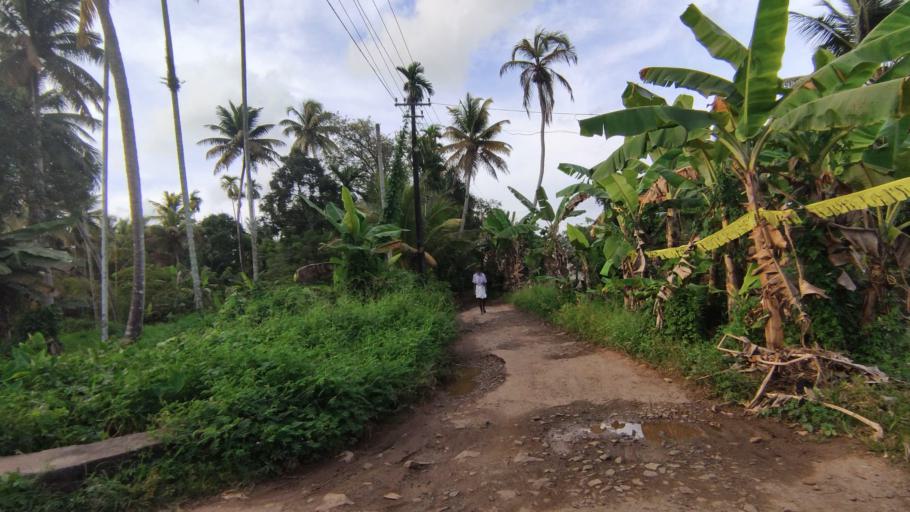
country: IN
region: Kerala
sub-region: Kottayam
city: Kottayam
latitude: 9.6022
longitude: 76.4398
